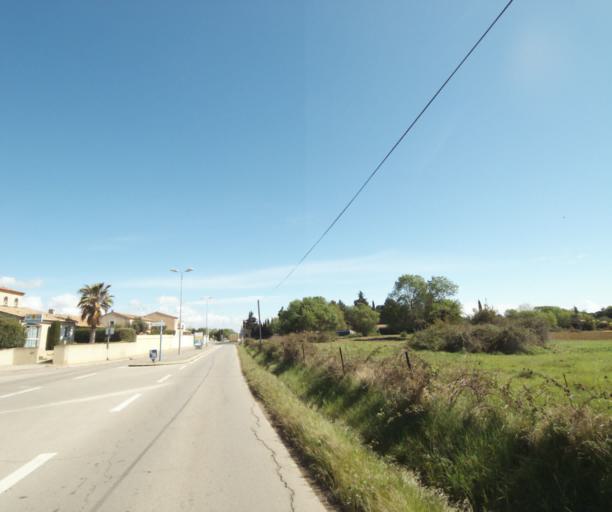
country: FR
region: Languedoc-Roussillon
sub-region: Departement de l'Herault
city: Villeneuve-les-Maguelone
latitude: 43.5370
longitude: 3.8682
